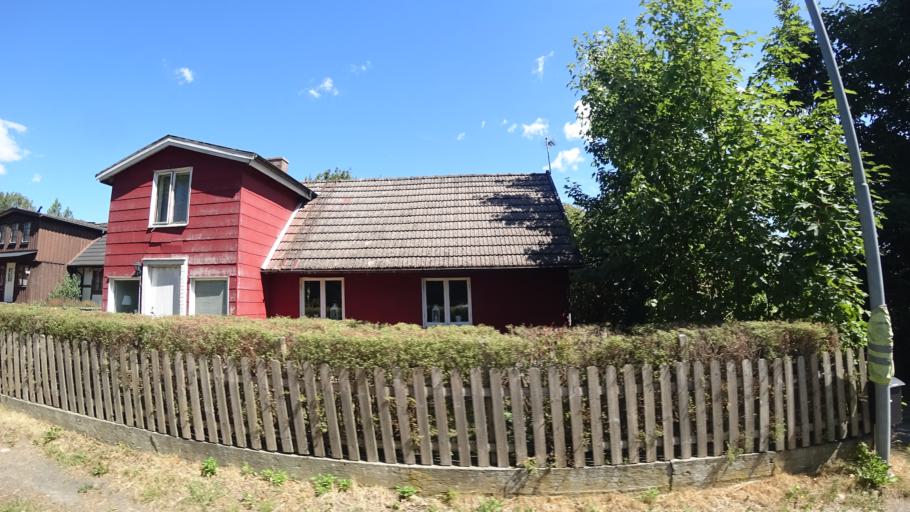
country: SE
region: Skane
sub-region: Kristianstads Kommun
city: Onnestad
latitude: 56.0477
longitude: 14.0250
